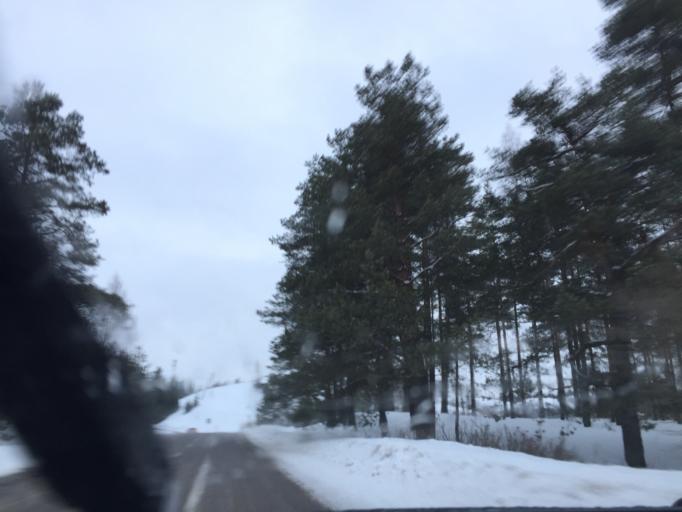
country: LV
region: Amatas Novads
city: Drabesi
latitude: 57.2102
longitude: 25.3043
